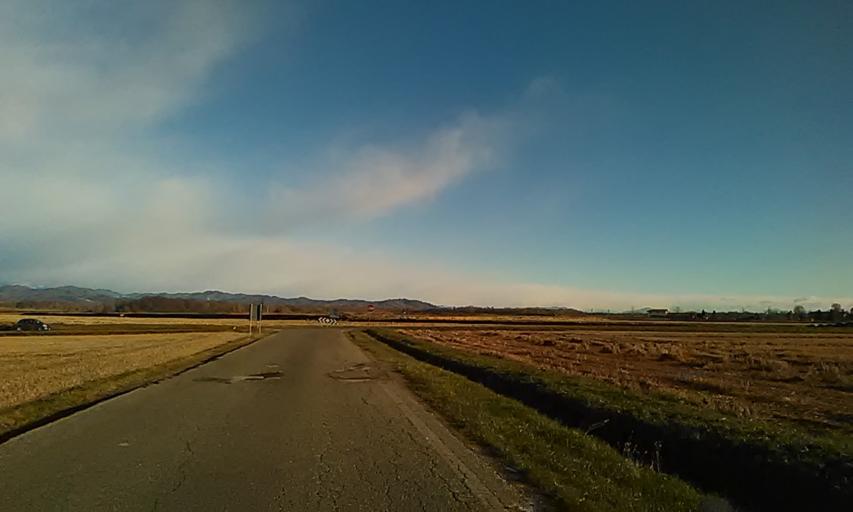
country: IT
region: Piedmont
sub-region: Provincia di Vercelli
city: Rovasenda
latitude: 45.5454
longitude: 8.2774
